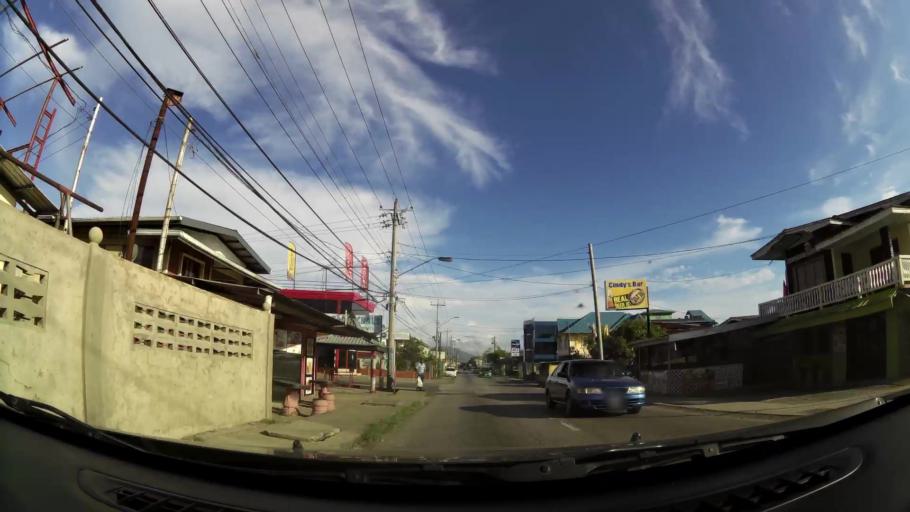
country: TT
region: Chaguanas
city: Chaguanas
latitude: 10.5589
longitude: -61.3731
